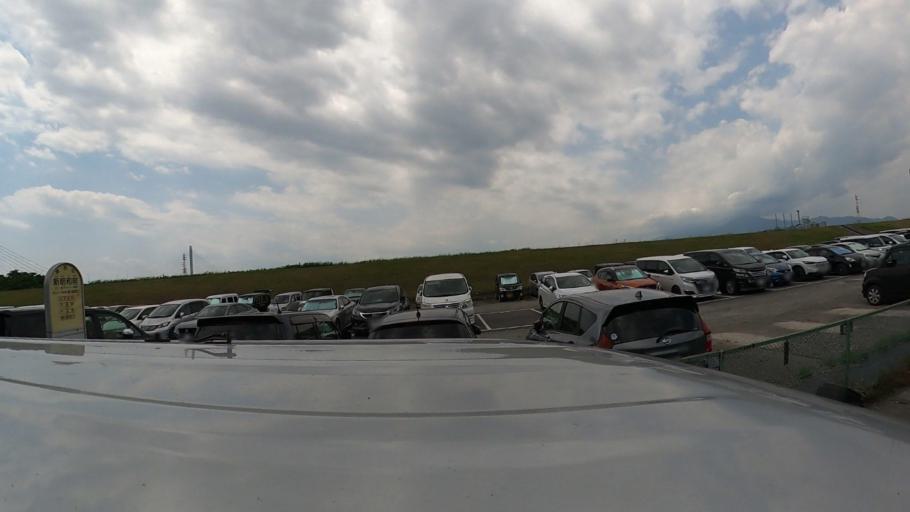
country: JP
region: Kanagawa
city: Chigasaki
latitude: 35.3563
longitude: 139.3731
